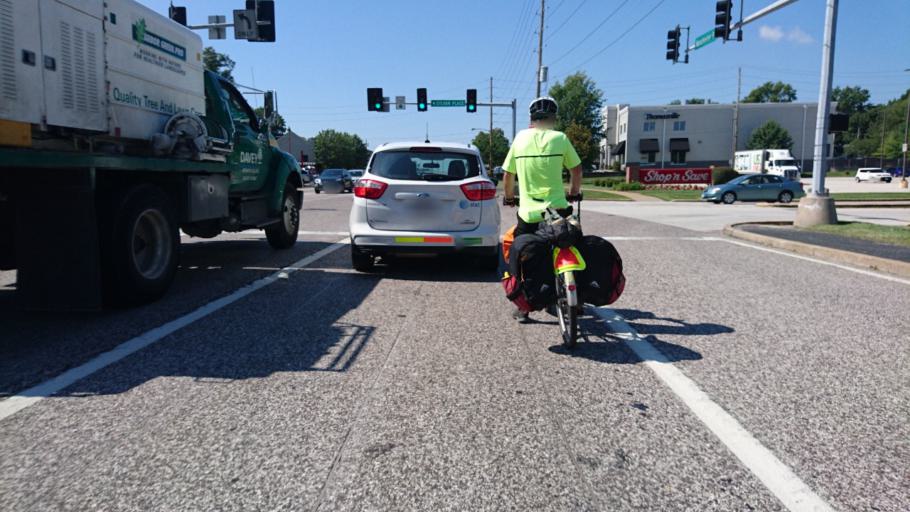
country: US
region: Missouri
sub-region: Saint Louis County
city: Warson Woods
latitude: 38.6007
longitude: -90.4005
